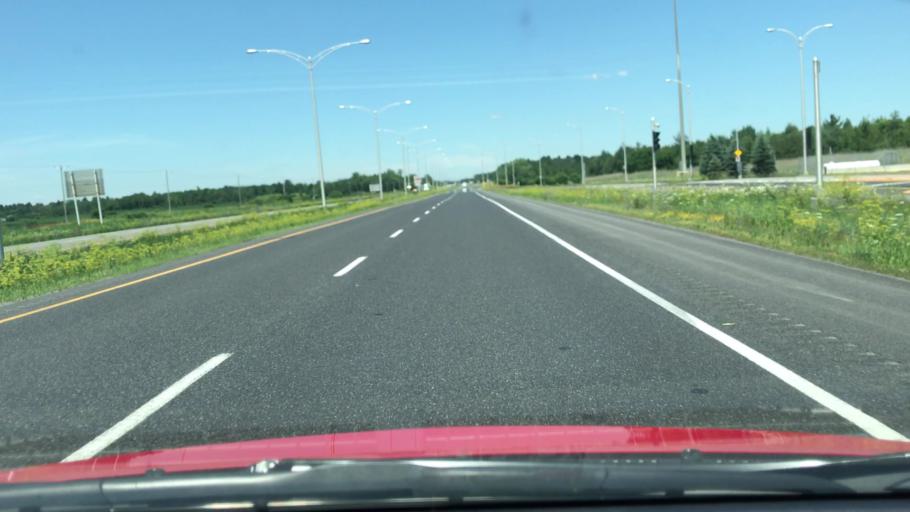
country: US
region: New York
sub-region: Clinton County
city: Champlain
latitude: 45.0357
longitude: -73.4534
